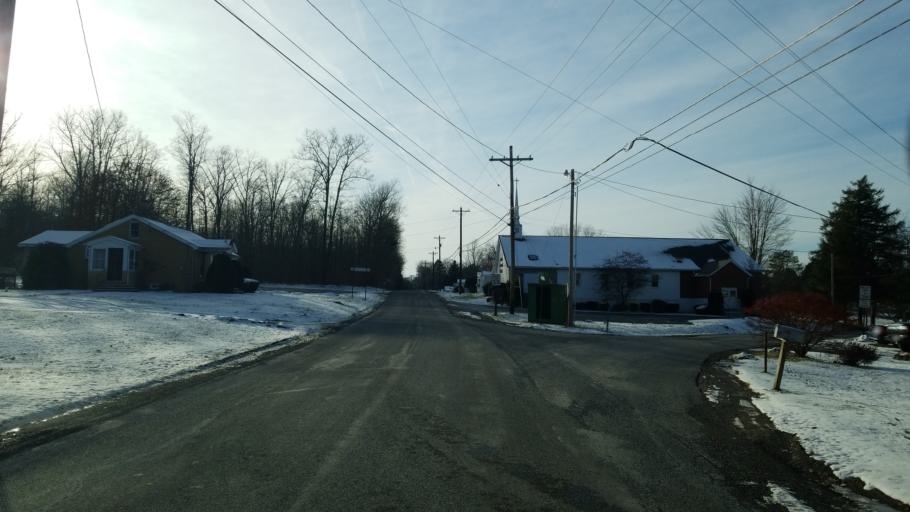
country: US
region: Pennsylvania
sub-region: Clearfield County
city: DuBois
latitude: 41.1092
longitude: -78.6961
